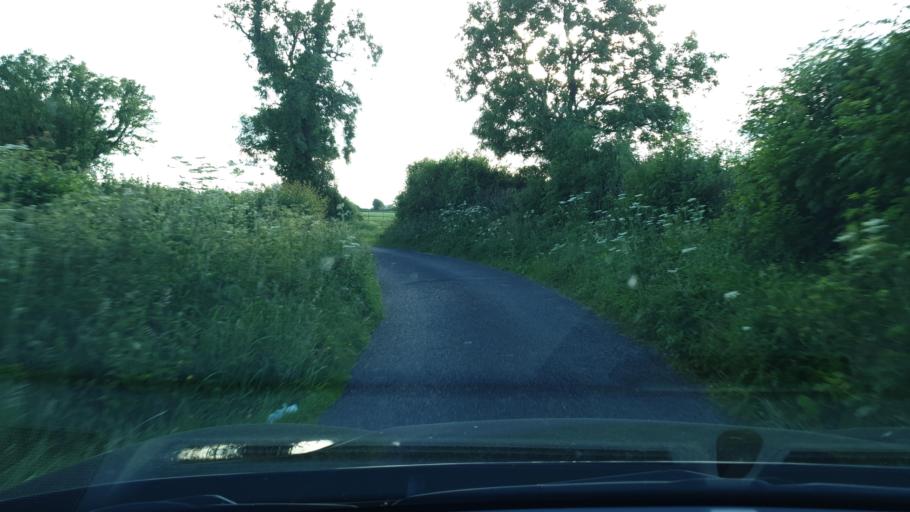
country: IE
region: Leinster
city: Hartstown
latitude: 53.4474
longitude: -6.4032
